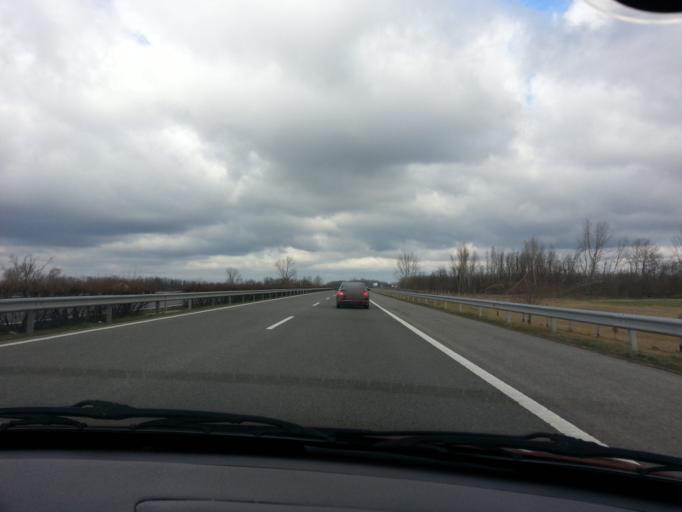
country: HU
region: Csongrad
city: Csengele
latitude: 46.5335
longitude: 19.8903
